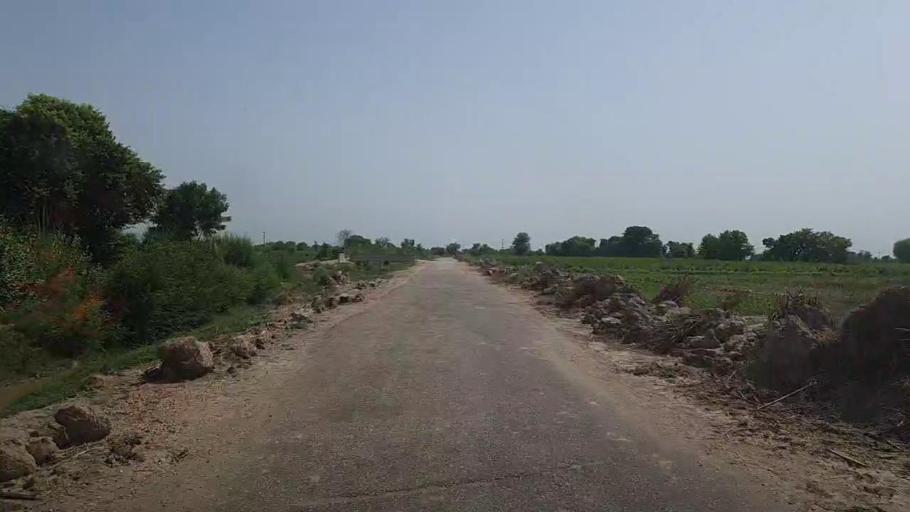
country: PK
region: Sindh
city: Pad Idan
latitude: 26.8281
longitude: 68.3296
